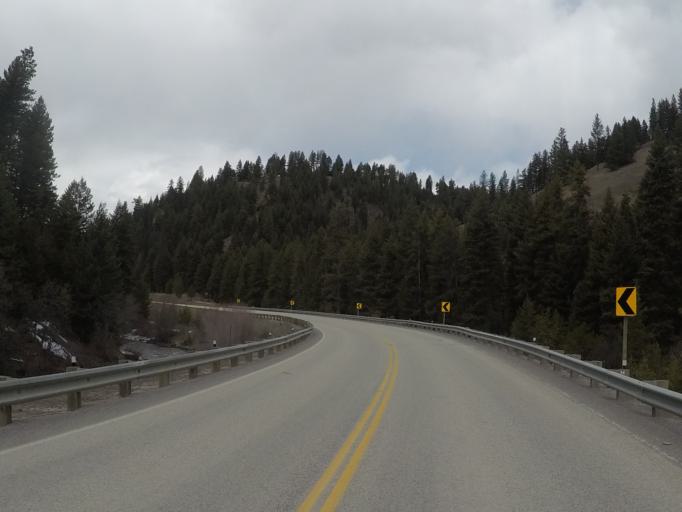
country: US
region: Montana
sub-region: Missoula County
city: Lolo
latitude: 46.7702
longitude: -114.3522
